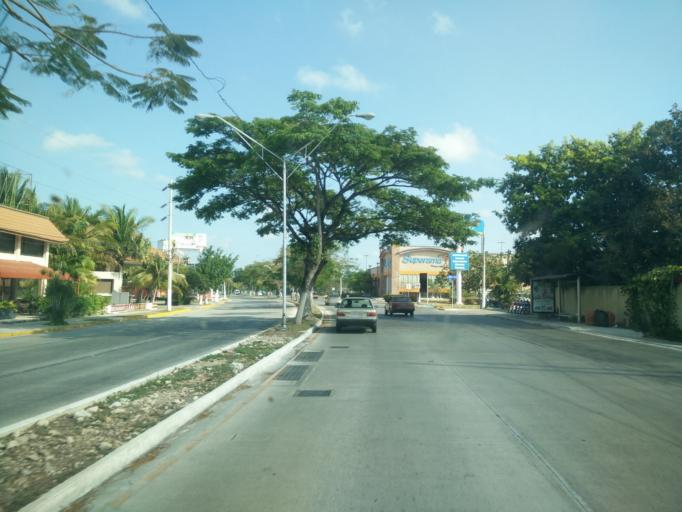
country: MX
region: Yucatan
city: Merida
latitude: 21.0125
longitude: -89.6135
